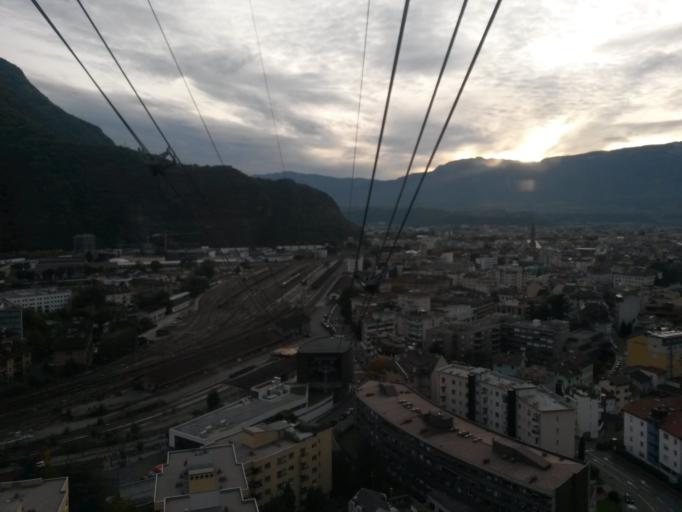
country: IT
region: Trentino-Alto Adige
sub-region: Bolzano
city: Cardano
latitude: 46.5013
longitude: 11.3661
